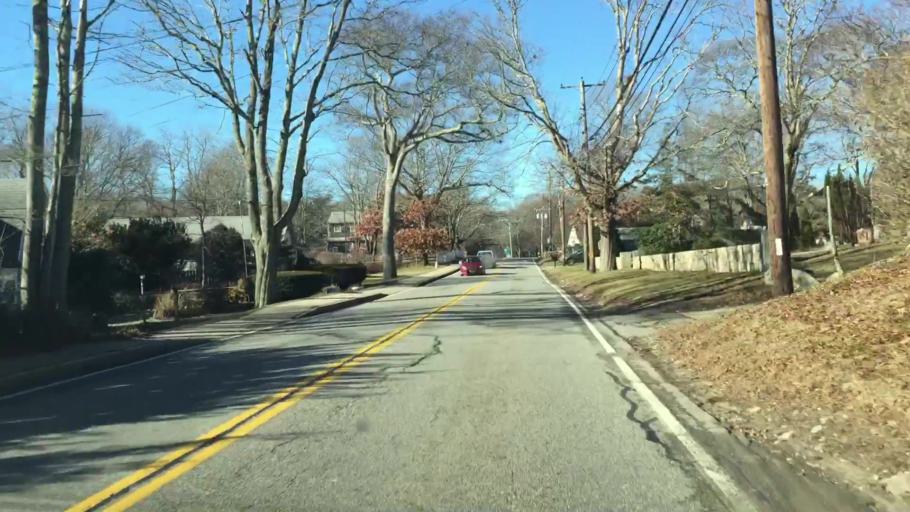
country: US
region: Massachusetts
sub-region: Barnstable County
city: Falmouth
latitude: 41.5633
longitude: -70.6163
